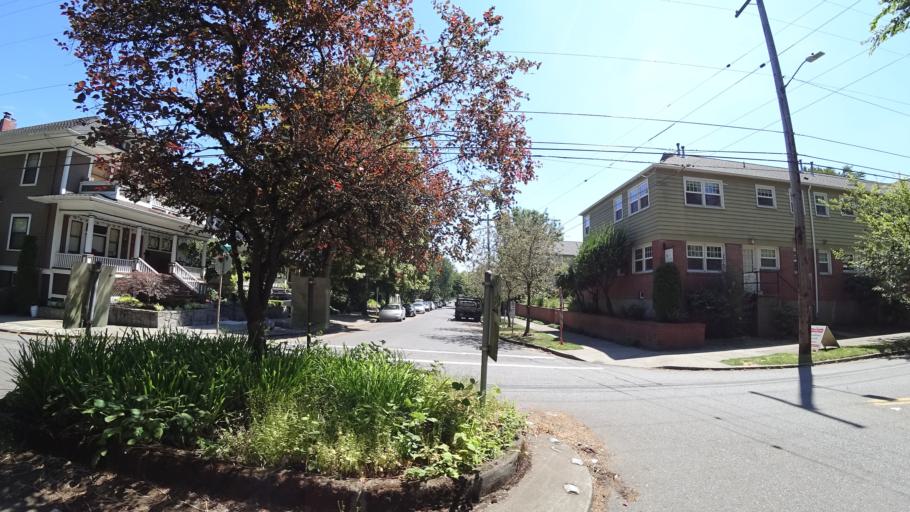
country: US
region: Oregon
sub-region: Multnomah County
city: Portland
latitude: 45.5333
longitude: -122.7028
